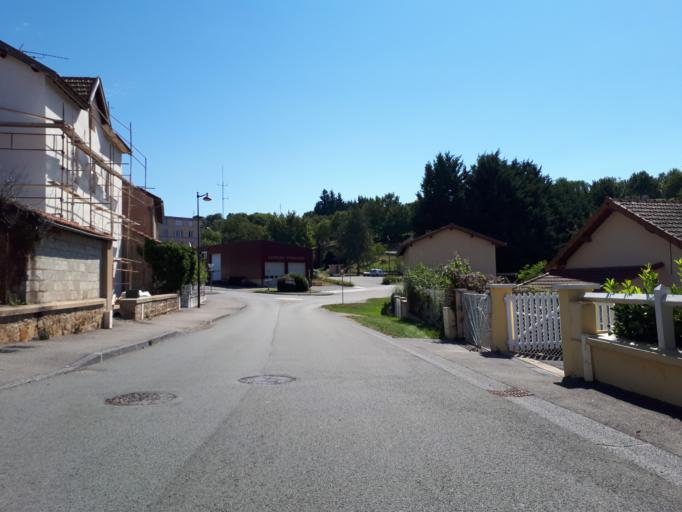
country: FR
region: Rhone-Alpes
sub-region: Departement de la Loire
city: Bussieres
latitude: 45.8355
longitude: 4.2707
